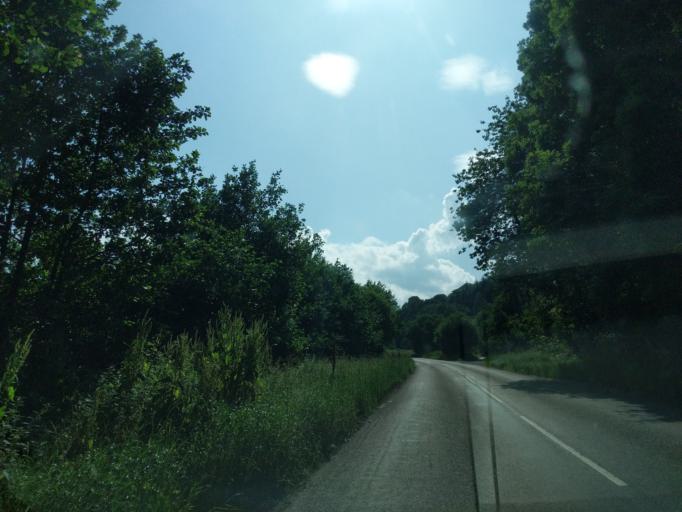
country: GB
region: Scotland
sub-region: Moray
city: Rothes
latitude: 57.5390
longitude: -3.1998
